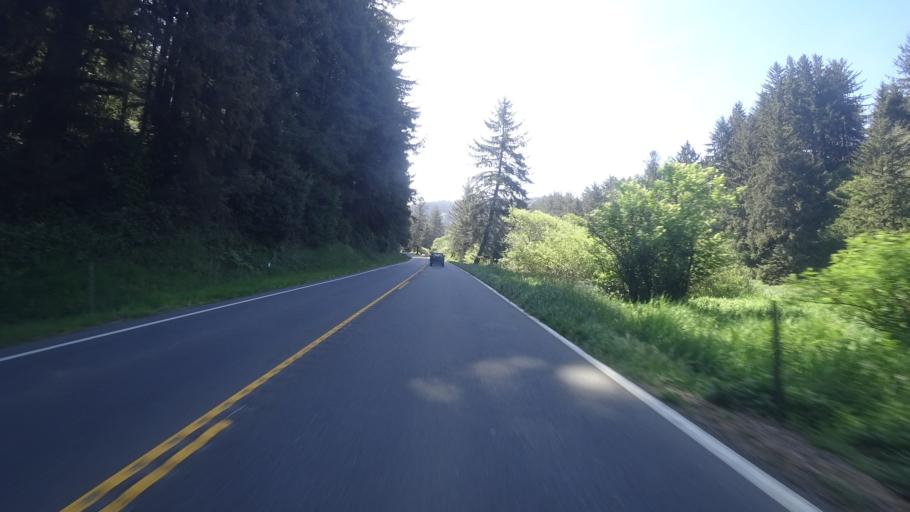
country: US
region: California
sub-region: Del Norte County
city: Bertsch-Oceanview
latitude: 41.5907
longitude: -124.0961
